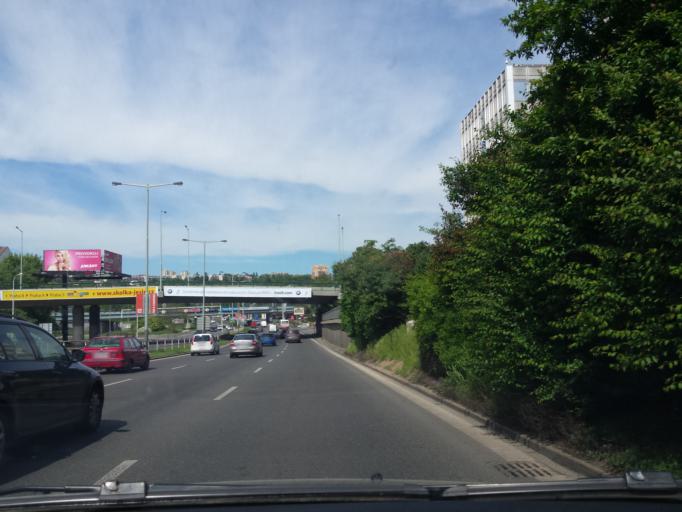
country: CZ
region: Praha
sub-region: Praha 8
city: Karlin
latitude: 50.1088
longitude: 14.4441
